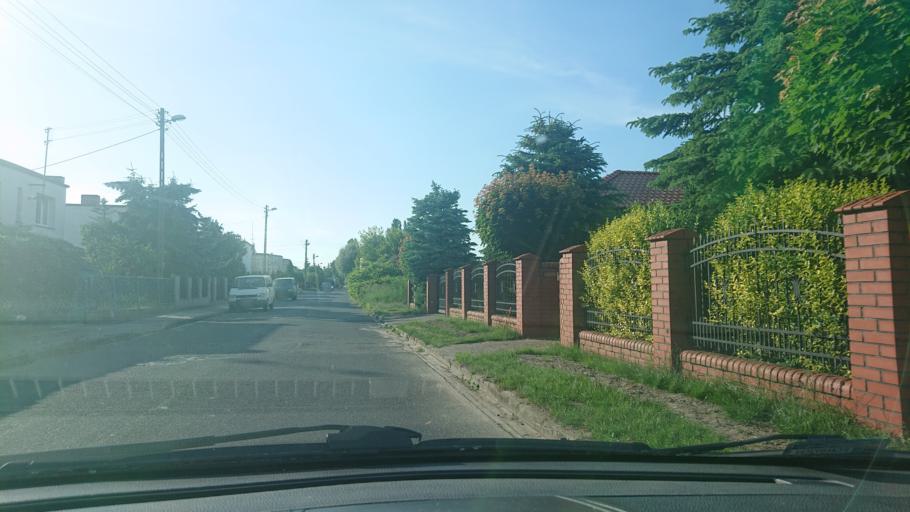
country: PL
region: Greater Poland Voivodeship
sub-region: Powiat gnieznienski
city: Gniezno
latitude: 52.5228
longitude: 17.6071
